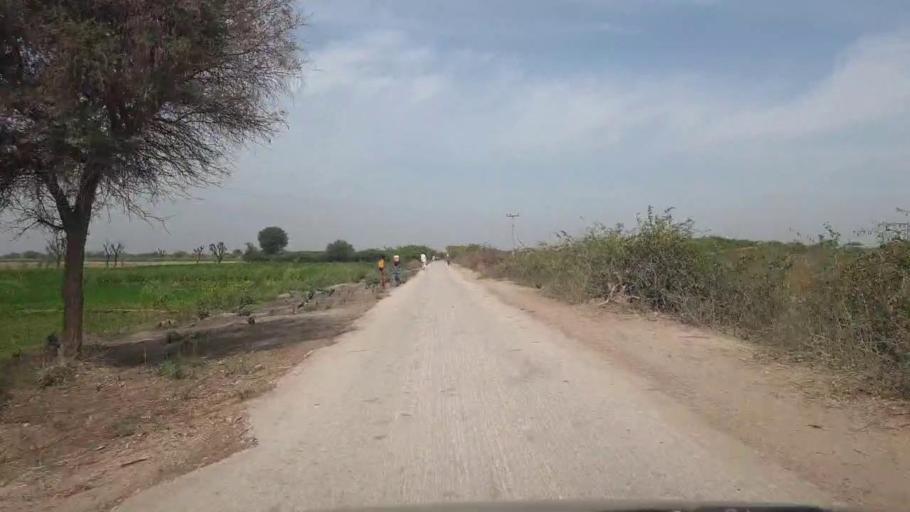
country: PK
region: Sindh
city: Kunri
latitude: 25.2331
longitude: 69.6704
